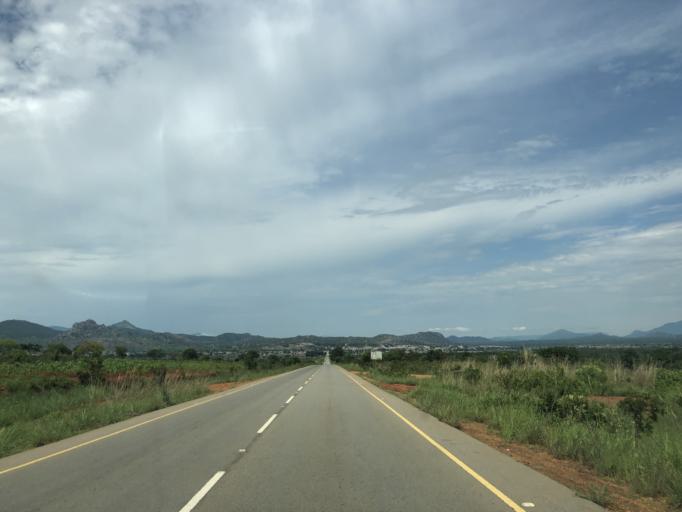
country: AO
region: Cuanza Sul
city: Quibala
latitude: -10.7336
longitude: 15.0147
